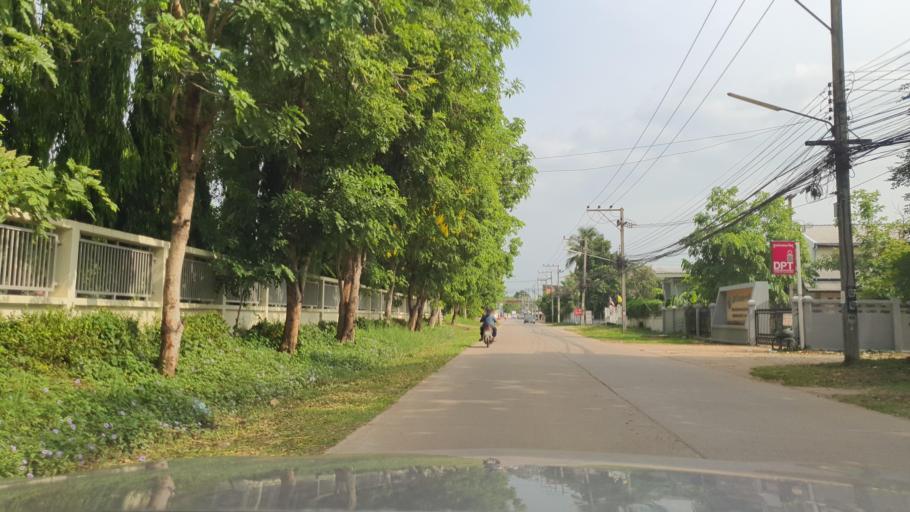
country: TH
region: Phitsanulok
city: Phitsanulok
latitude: 16.8462
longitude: 100.2576
